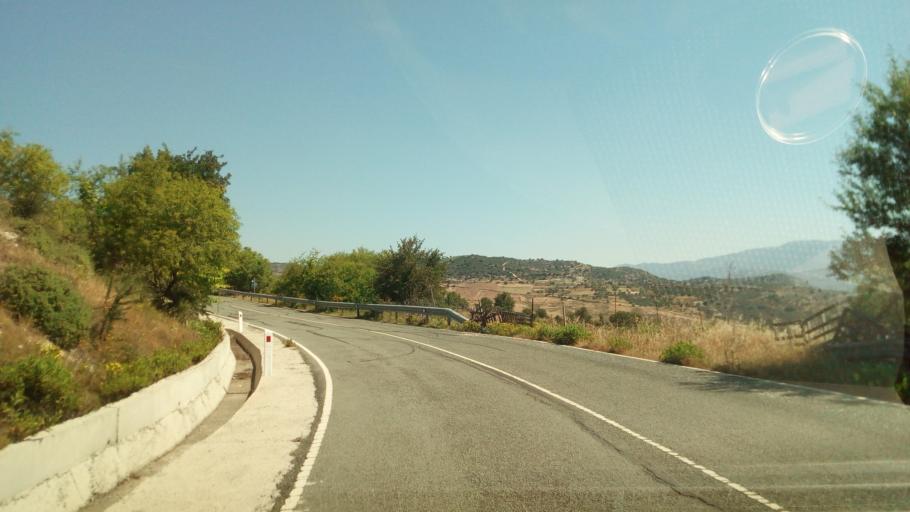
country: CY
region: Limassol
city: Pachna
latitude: 34.8127
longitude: 32.6816
